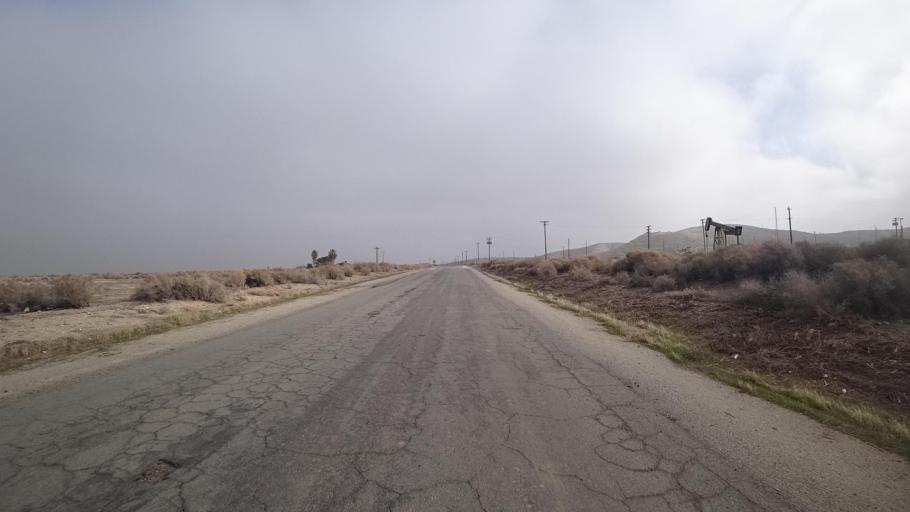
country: US
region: California
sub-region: Kern County
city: Maricopa
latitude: 35.0379
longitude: -119.3687
